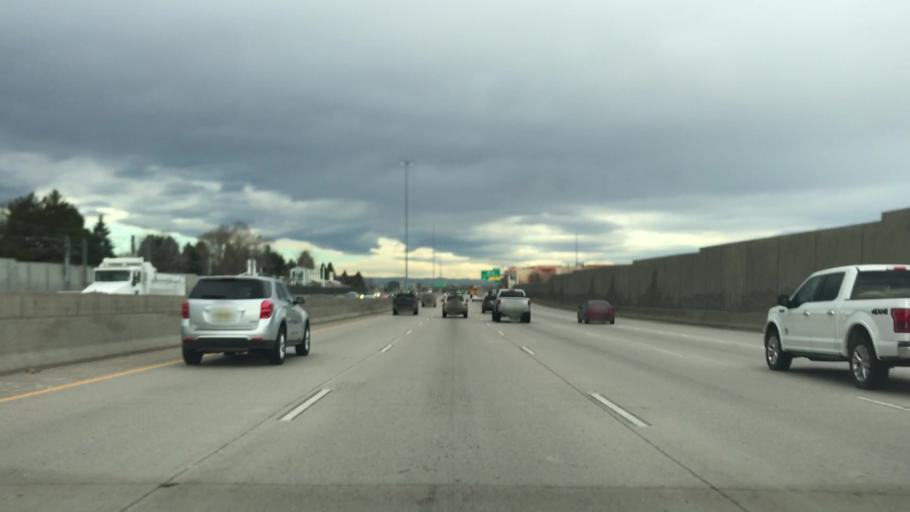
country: US
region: Colorado
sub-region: Arapahoe County
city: Cherry Hills Village
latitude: 39.6499
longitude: -104.9147
